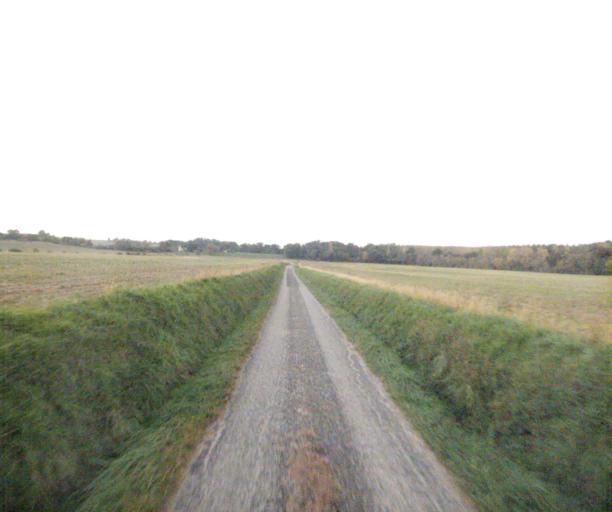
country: FR
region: Midi-Pyrenees
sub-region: Departement du Gers
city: Gondrin
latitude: 43.8143
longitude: 0.2527
